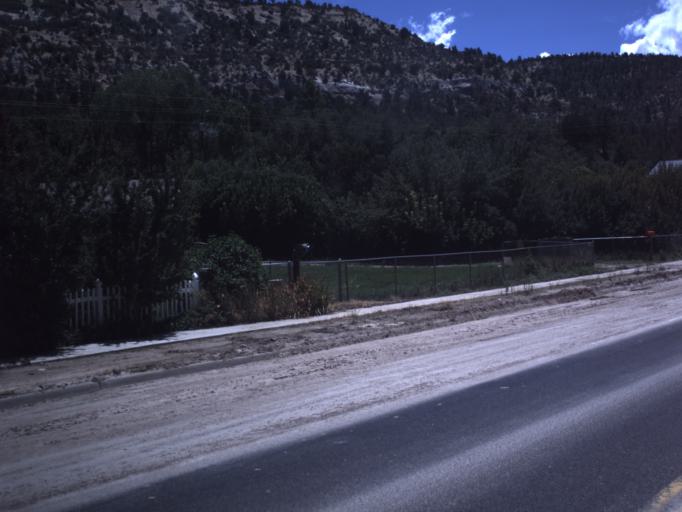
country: US
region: Utah
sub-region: Kane County
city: Kanab
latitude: 37.3130
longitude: -112.5975
